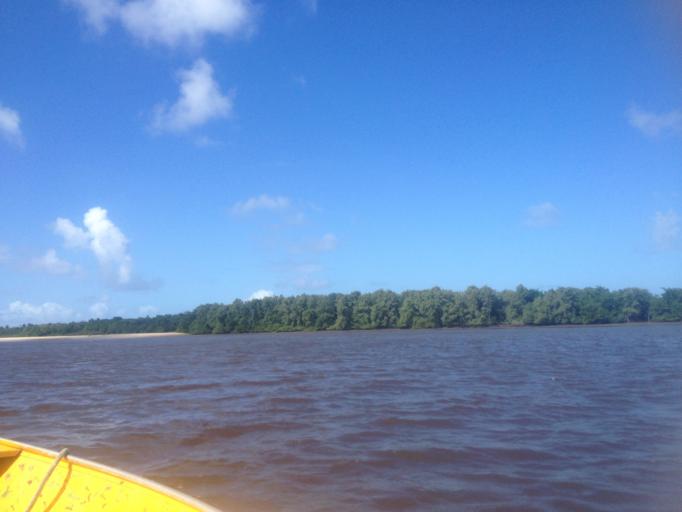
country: BR
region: Sergipe
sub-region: Indiaroba
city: Indiaroba
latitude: -11.4784
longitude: -37.3876
